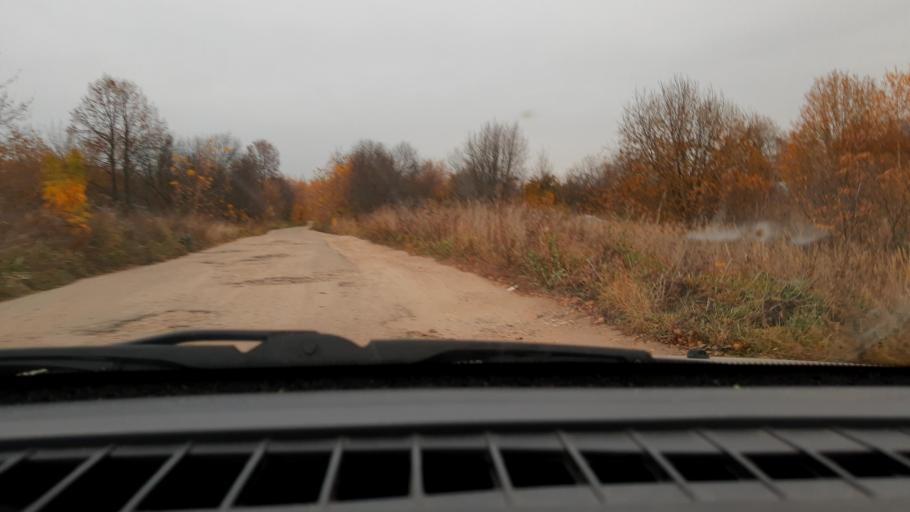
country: RU
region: Nizjnij Novgorod
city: Burevestnik
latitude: 56.0468
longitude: 43.8433
